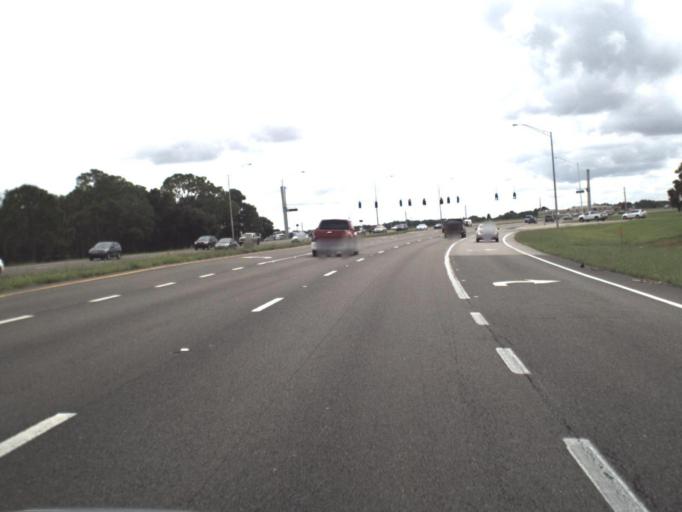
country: US
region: Florida
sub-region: Manatee County
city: Samoset
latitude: 27.4670
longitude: -82.5333
